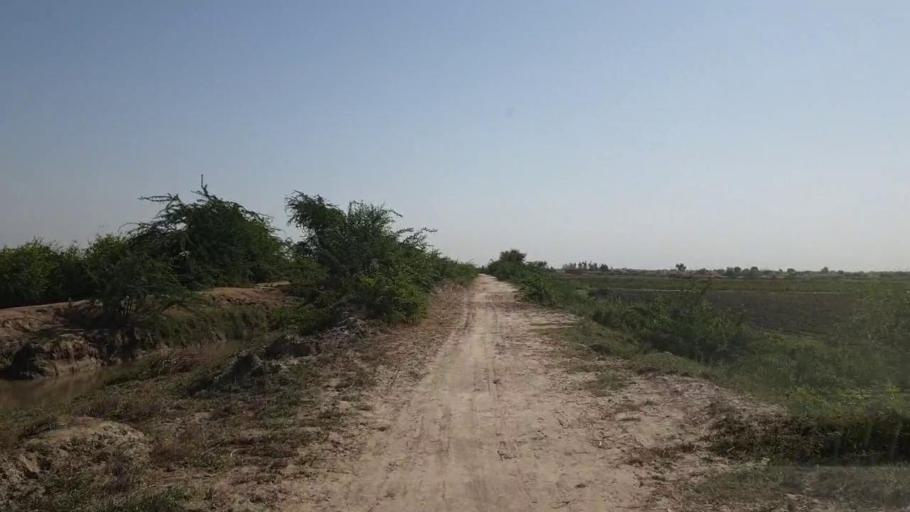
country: PK
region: Sindh
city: Kadhan
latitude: 24.6134
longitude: 68.9984
